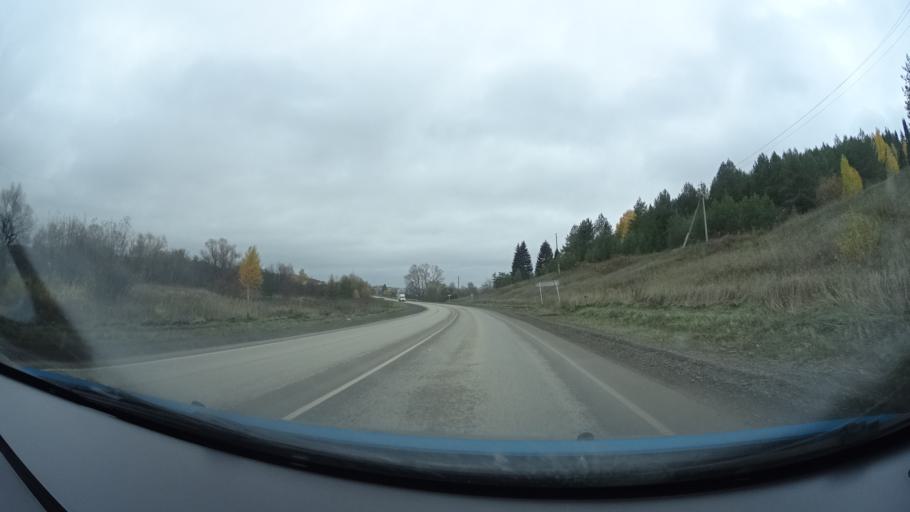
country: RU
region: Perm
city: Osa
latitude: 57.2268
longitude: 55.5882
